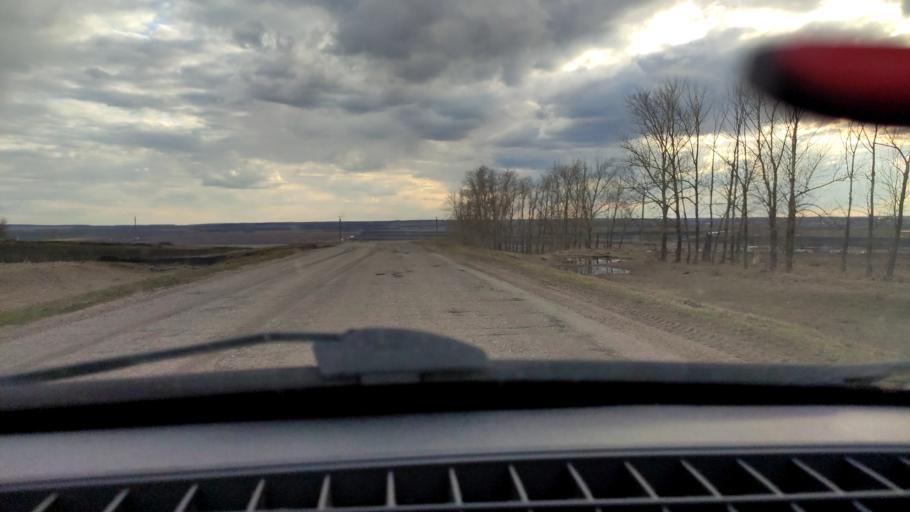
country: RU
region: Bashkortostan
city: Karmaskaly
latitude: 54.3000
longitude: 55.9245
